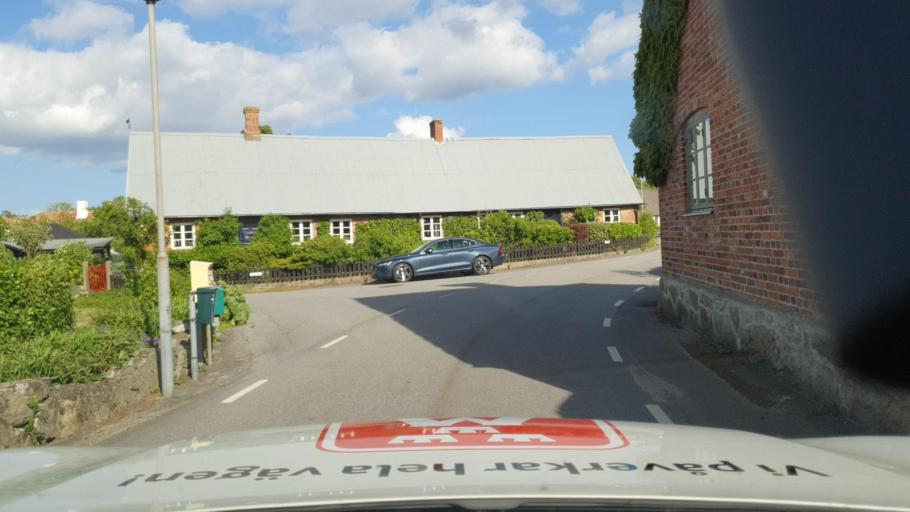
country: SE
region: Skane
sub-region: Simrishamns Kommun
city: Kivik
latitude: 55.6147
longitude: 14.2889
